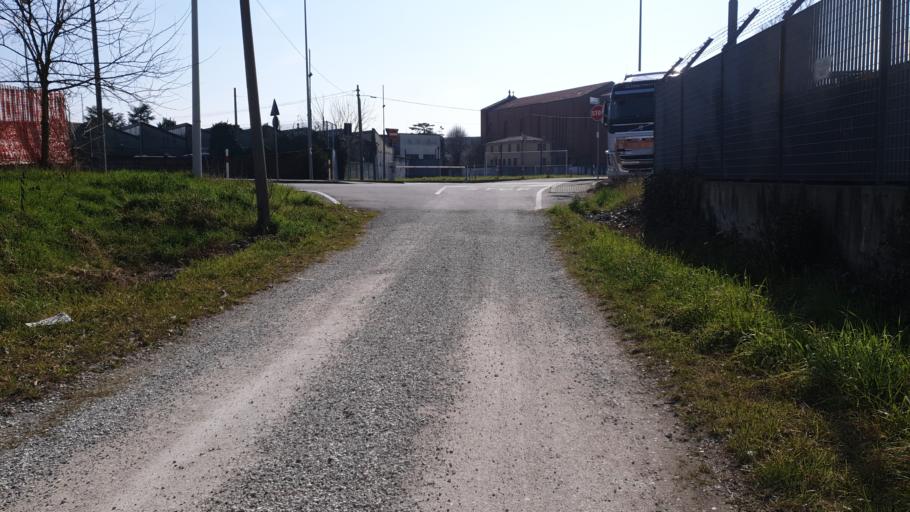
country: IT
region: Veneto
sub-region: Provincia di Padova
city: Cadoneghe
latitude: 45.4168
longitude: 11.9170
